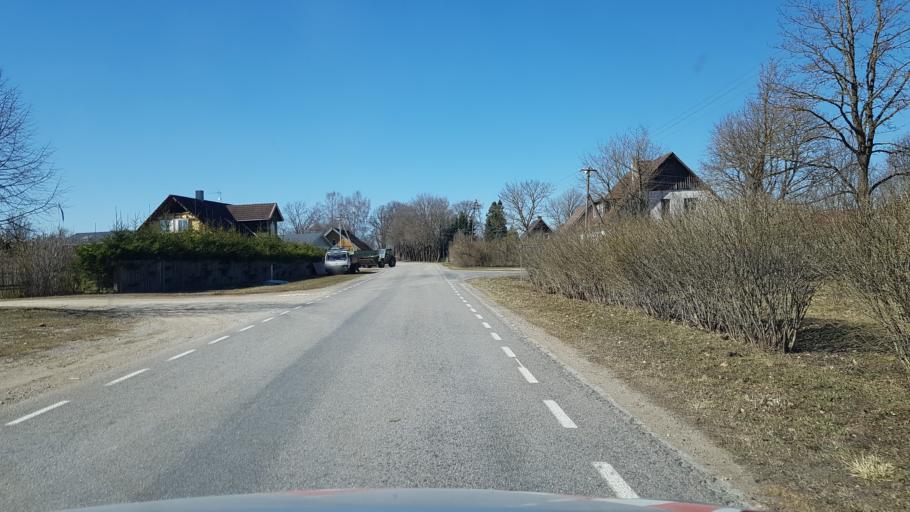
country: EE
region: Laeaene-Virumaa
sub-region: Vaeike-Maarja vald
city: Vaike-Maarja
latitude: 59.1122
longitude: 26.3725
